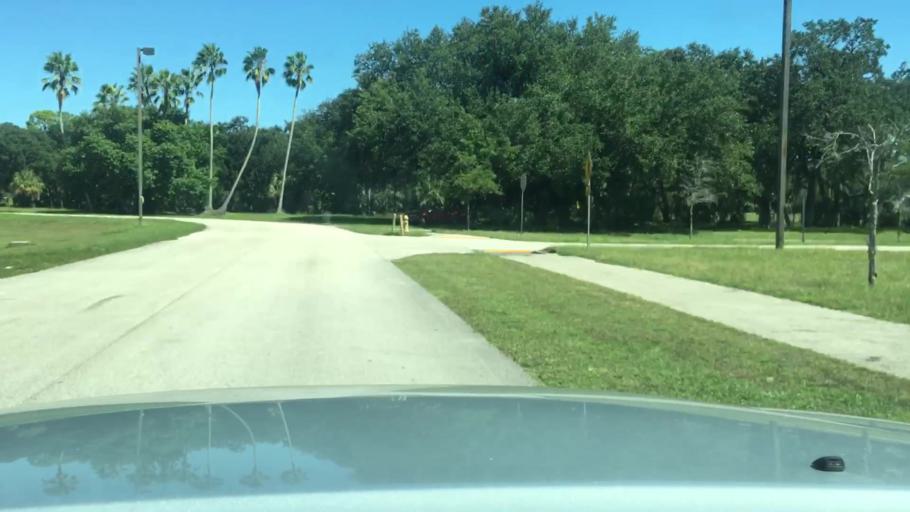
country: US
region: Florida
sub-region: Miami-Dade County
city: Ives Estates
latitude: 25.9693
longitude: -80.1697
